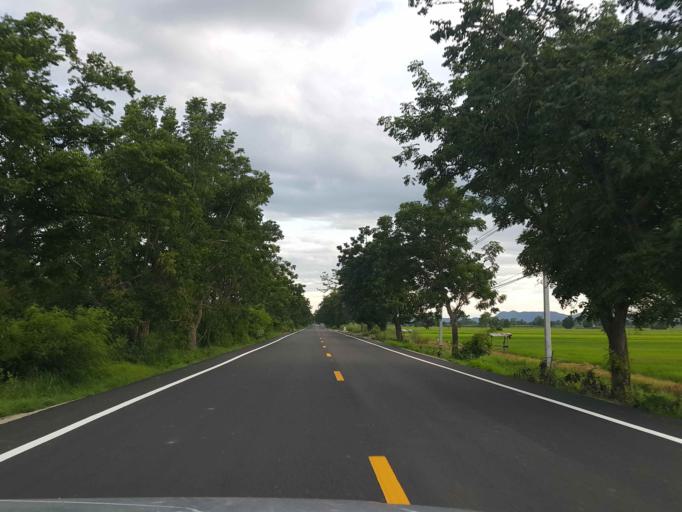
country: TH
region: Sukhothai
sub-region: Amphoe Si Satchanalai
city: Si Satchanalai
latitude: 17.4913
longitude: 99.7488
